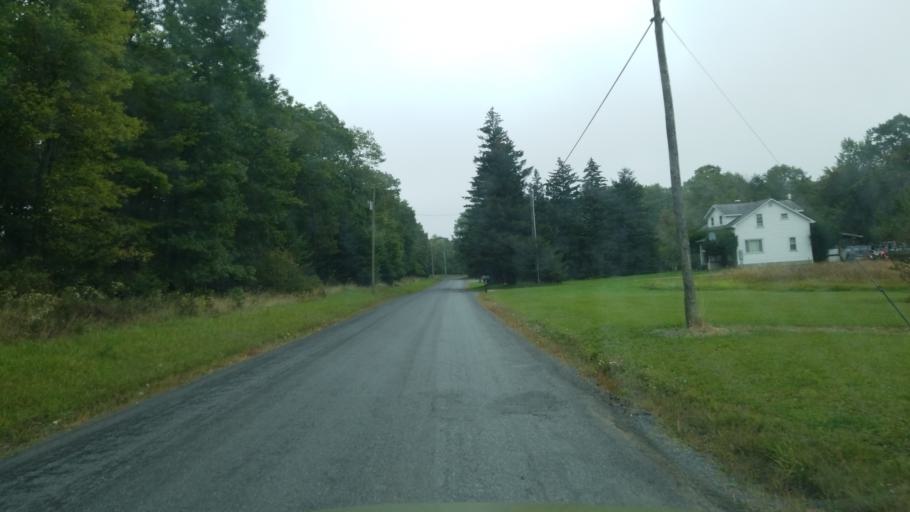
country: US
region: Pennsylvania
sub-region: Clearfield County
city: Curwensville
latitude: 41.0381
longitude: -78.5649
